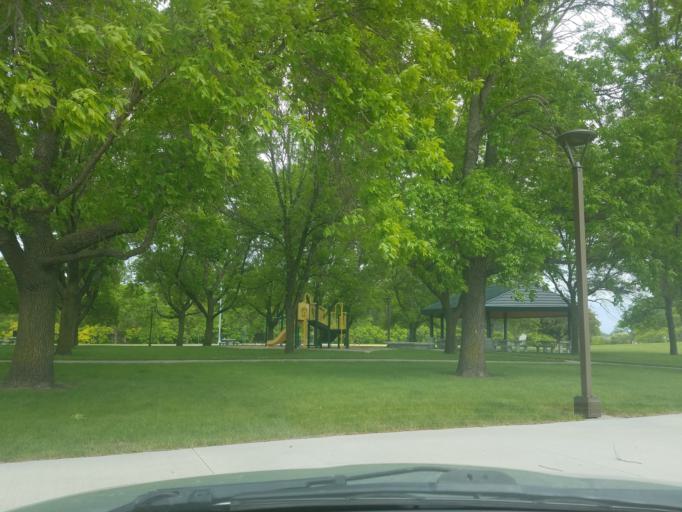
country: US
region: Minnesota
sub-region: Clay County
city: Moorhead
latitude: 46.8450
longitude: -96.7416
